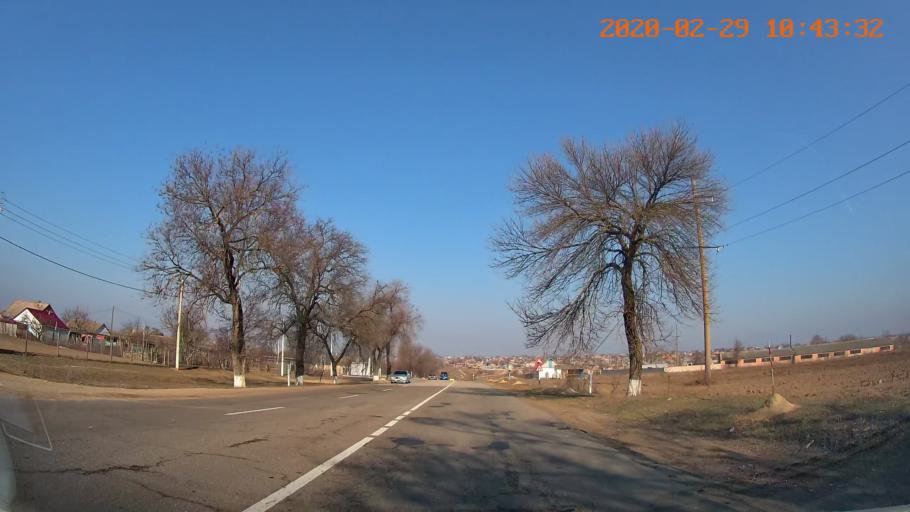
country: MD
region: Telenesti
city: Grigoriopol
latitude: 47.0623
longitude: 29.4030
